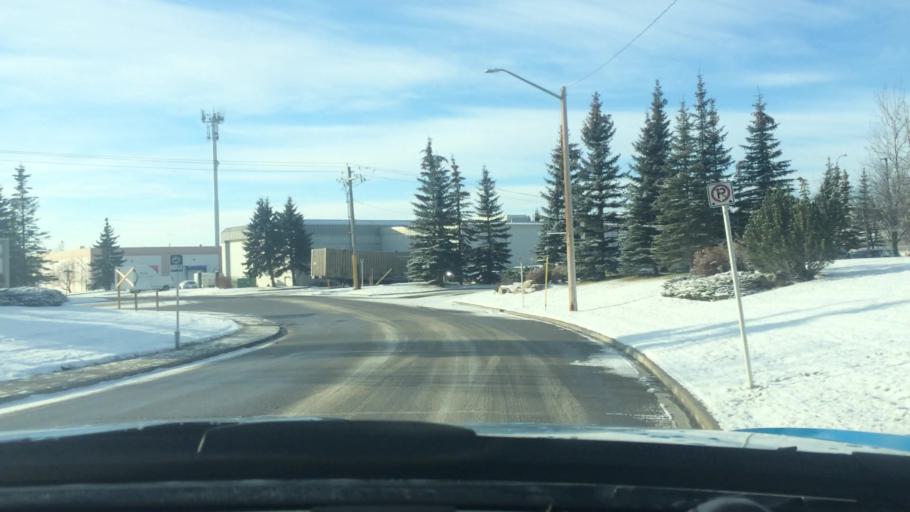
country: CA
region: Alberta
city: Calgary
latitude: 51.1184
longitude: -114.0442
